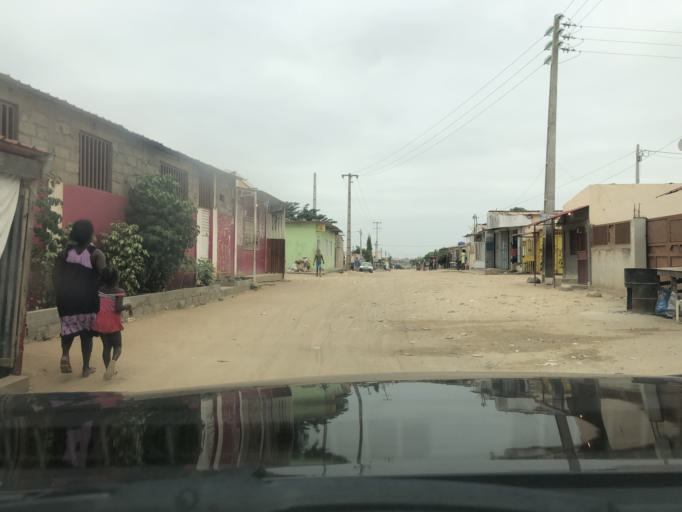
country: AO
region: Luanda
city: Luanda
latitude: -8.9376
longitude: 13.2308
